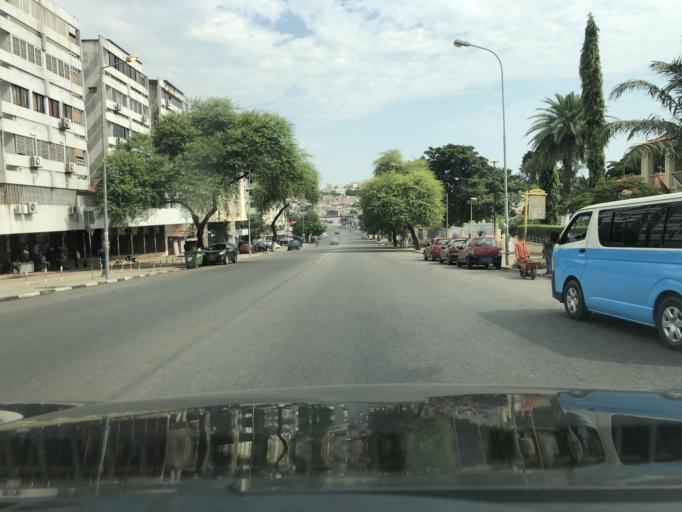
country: AO
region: Luanda
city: Luanda
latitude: -8.8268
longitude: 13.2272
